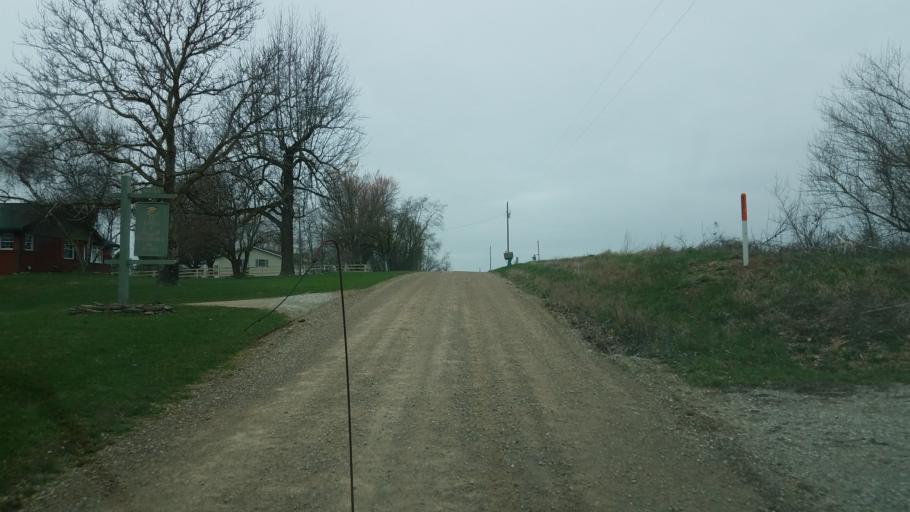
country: US
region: Ohio
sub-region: Knox County
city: Mount Vernon
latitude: 40.4650
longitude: -82.4368
